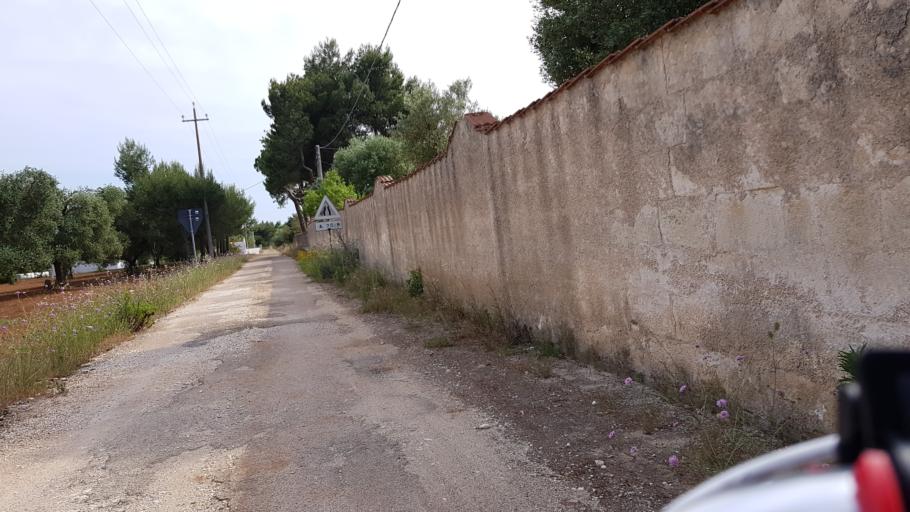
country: IT
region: Apulia
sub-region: Provincia di Brindisi
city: San Vito dei Normanni
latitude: 40.6532
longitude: 17.7713
